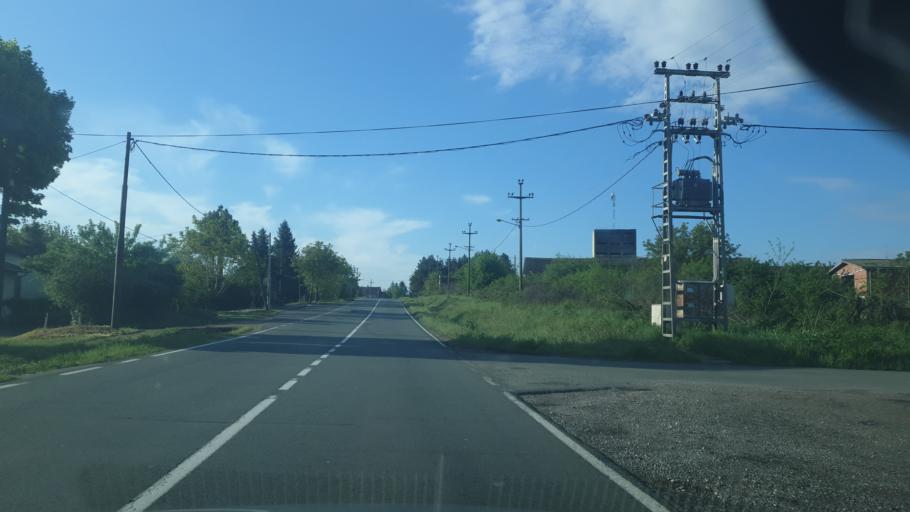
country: RS
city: Stubline
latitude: 44.5809
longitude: 20.1520
